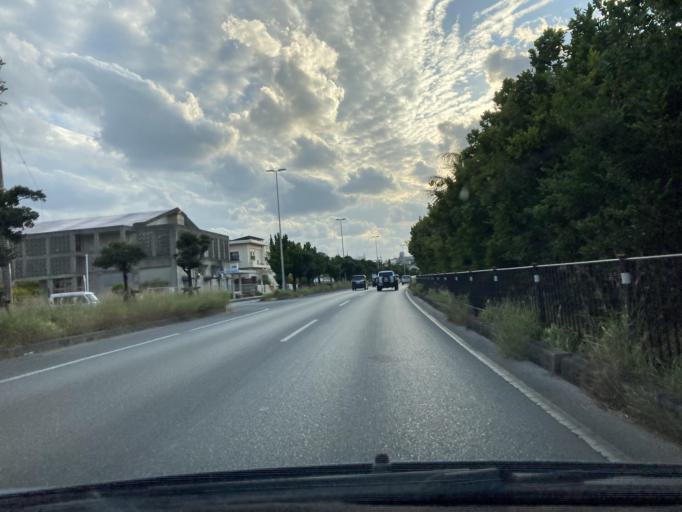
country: JP
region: Okinawa
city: Ginowan
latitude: 26.2811
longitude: 127.7418
